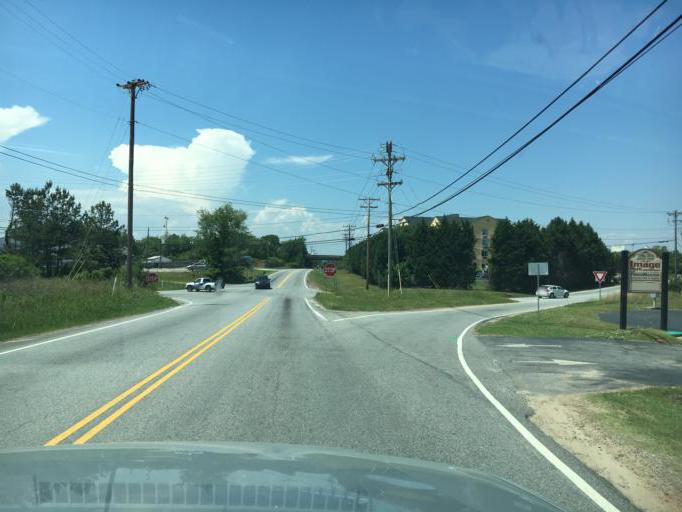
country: US
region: South Carolina
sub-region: Spartanburg County
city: Saxon
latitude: 34.9802
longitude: -81.9732
